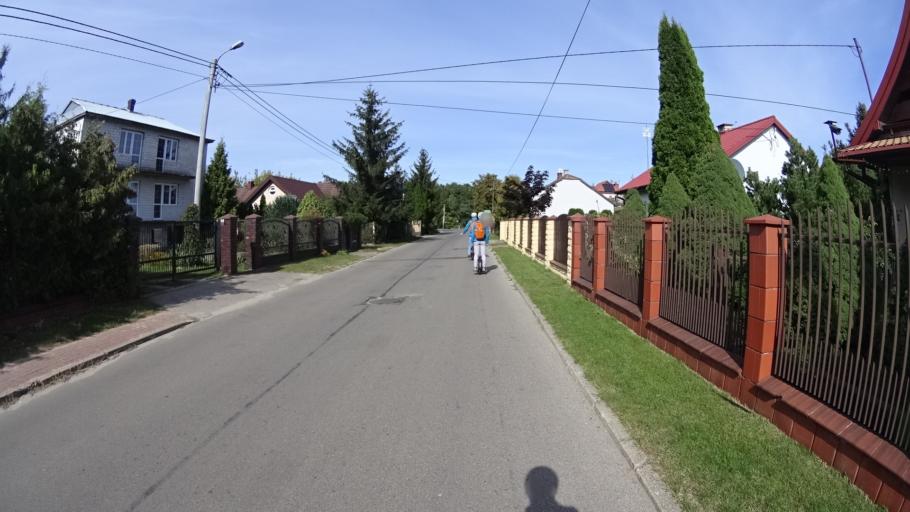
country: PL
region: Masovian Voivodeship
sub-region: Powiat legionowski
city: Bialobrzegi
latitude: 52.4727
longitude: 21.0691
